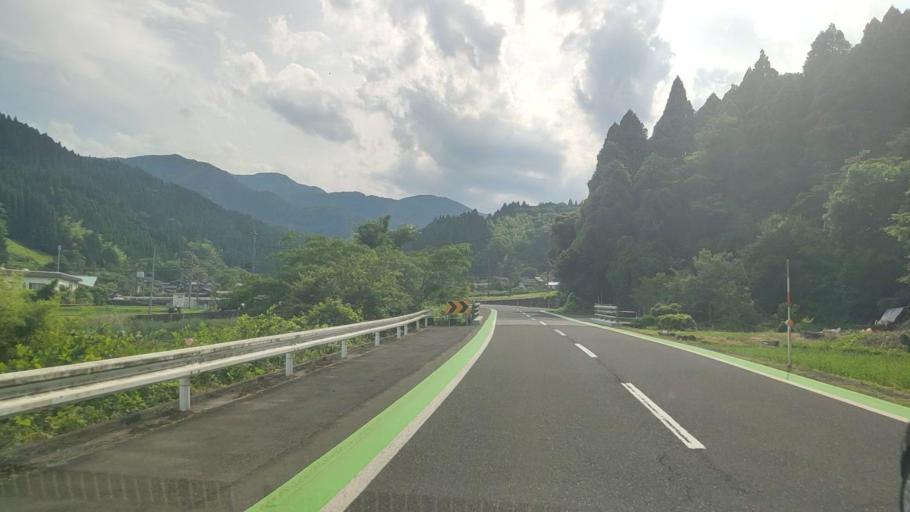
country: JP
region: Tottori
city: Tottori
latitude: 35.3309
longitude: 134.1007
